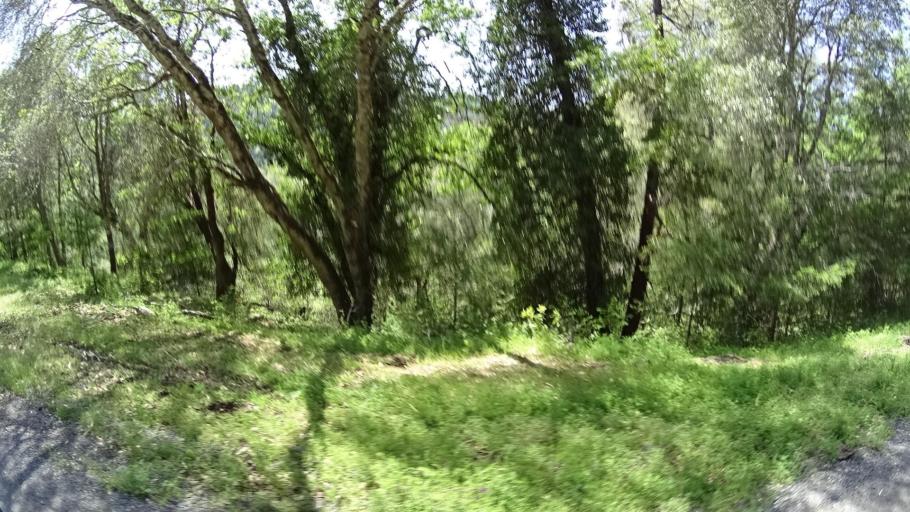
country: US
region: California
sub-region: Humboldt County
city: Redway
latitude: 40.2292
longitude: -123.6458
